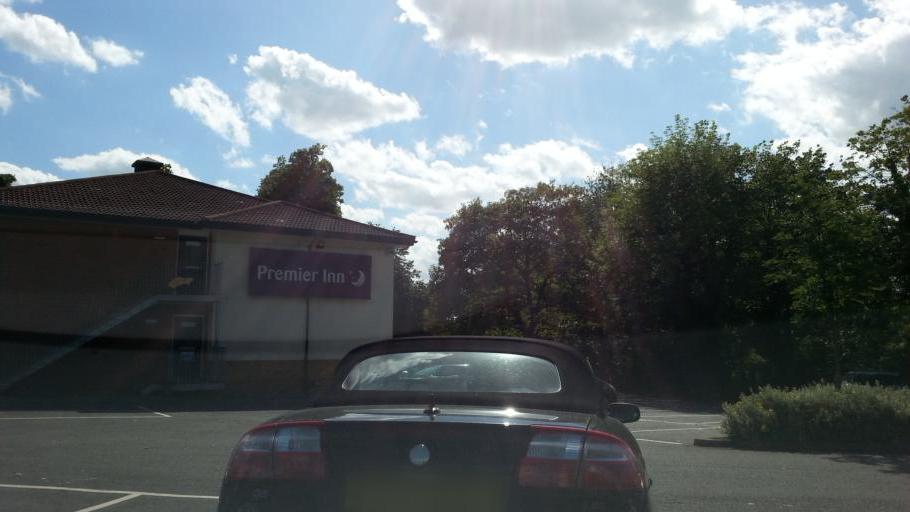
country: GB
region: England
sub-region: Nottinghamshire
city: Ruddington
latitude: 52.9086
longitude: -1.1453
